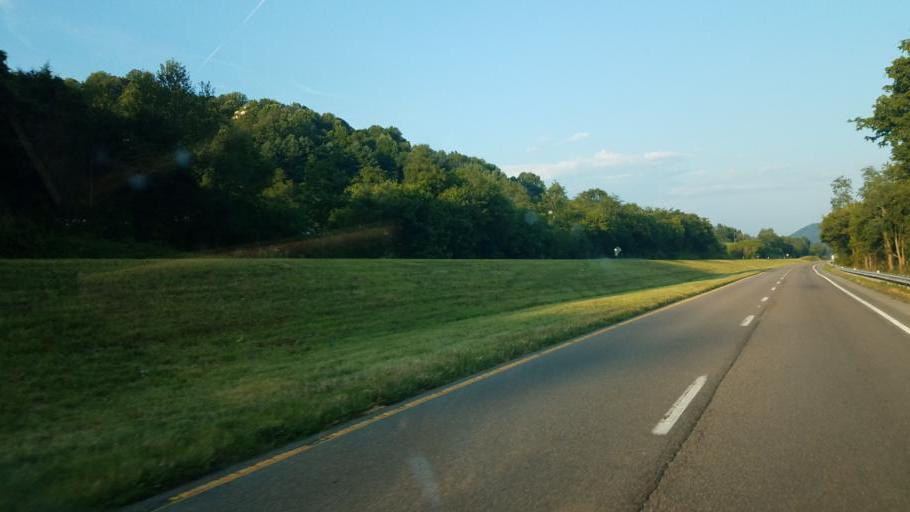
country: US
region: Virginia
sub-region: Scott County
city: Gate City
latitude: 36.6349
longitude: -82.6378
